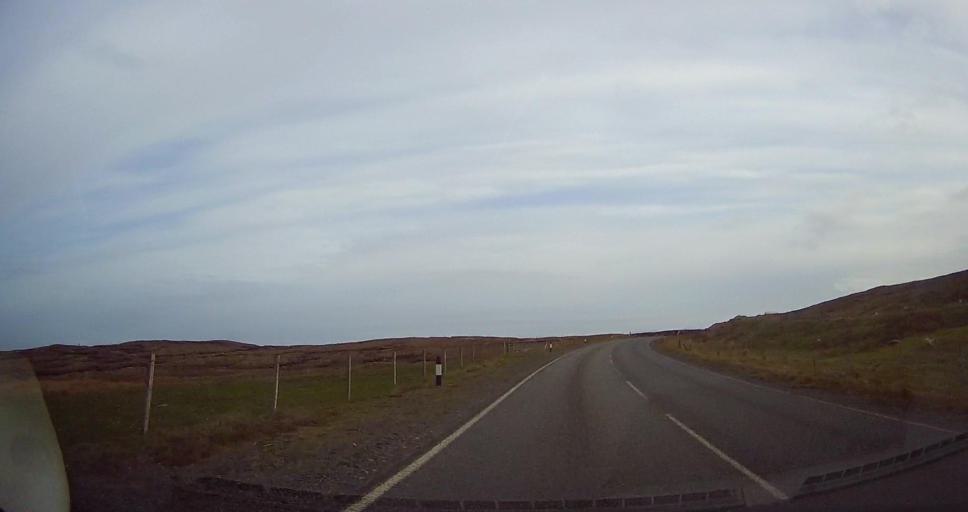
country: GB
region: Scotland
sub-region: Shetland Islands
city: Sandwick
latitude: 60.0920
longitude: -1.2287
